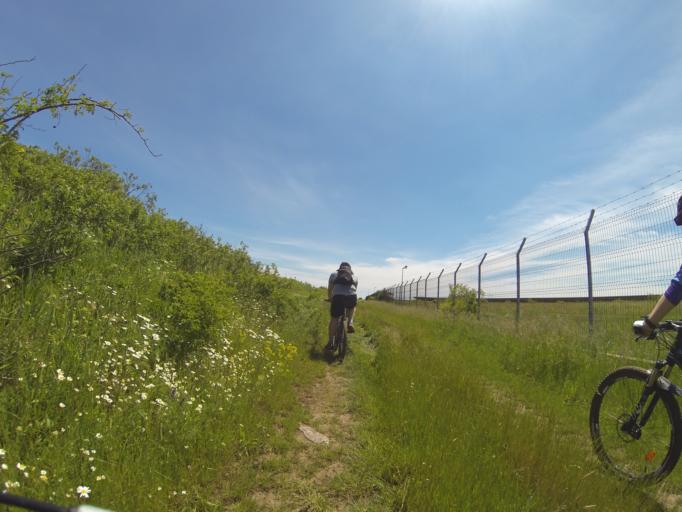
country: RO
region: Dolj
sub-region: Comuna Leu
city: Zanoaga
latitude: 44.1822
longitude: 24.0734
